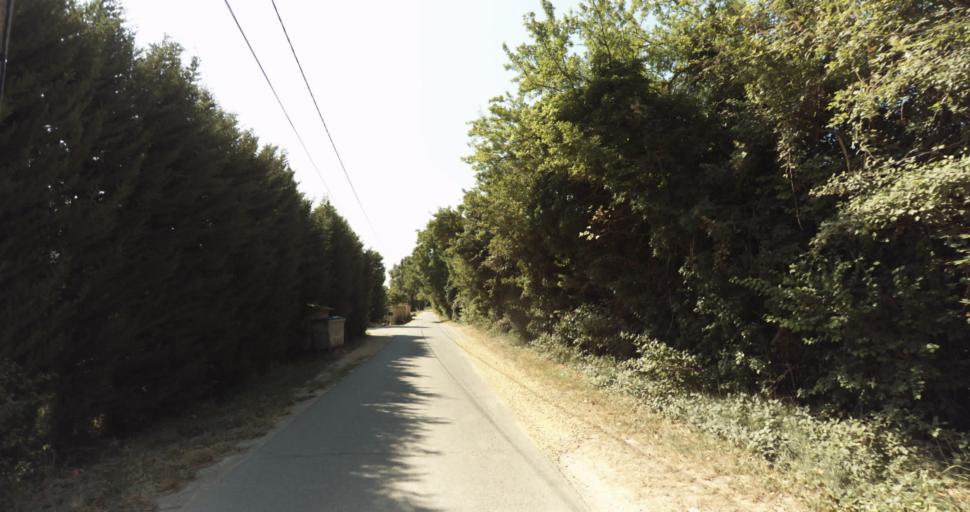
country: FR
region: Provence-Alpes-Cote d'Azur
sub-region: Departement du Vaucluse
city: Althen-des-Paluds
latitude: 44.0123
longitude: 4.9796
